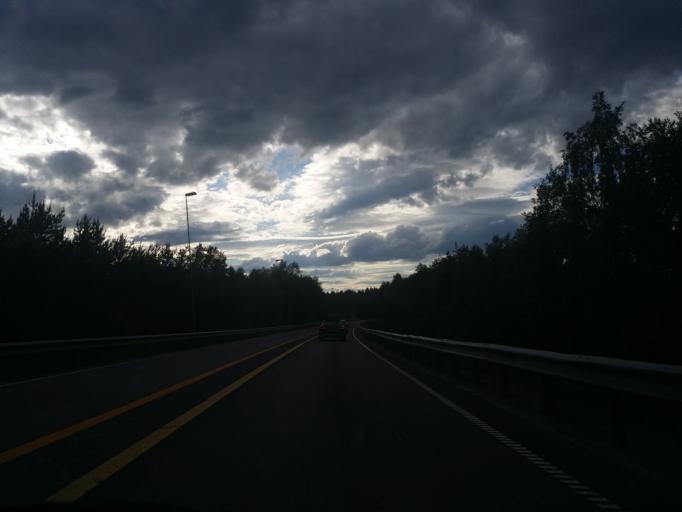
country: NO
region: Hedmark
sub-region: Ringsaker
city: Brumunddal
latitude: 60.8620
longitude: 10.9609
